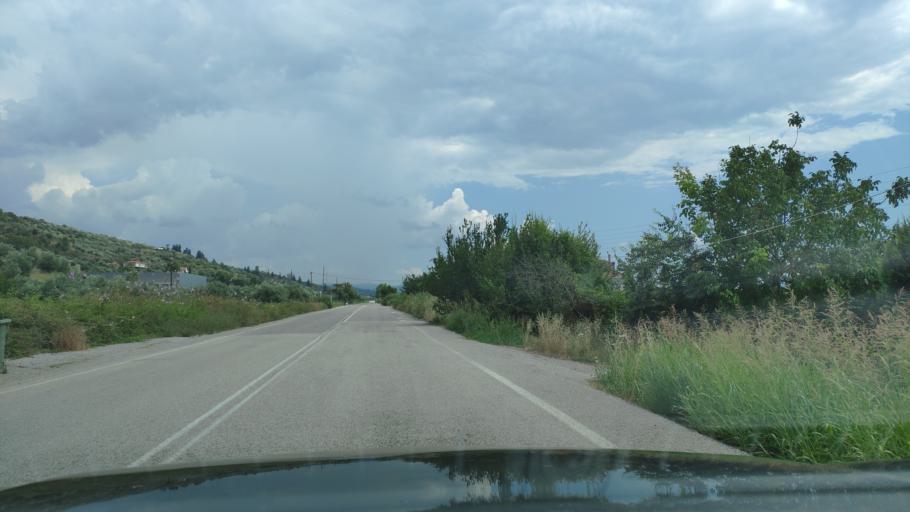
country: GR
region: West Greece
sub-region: Nomos Aitolias kai Akarnanias
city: Krikellos
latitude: 38.9650
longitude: 21.1694
